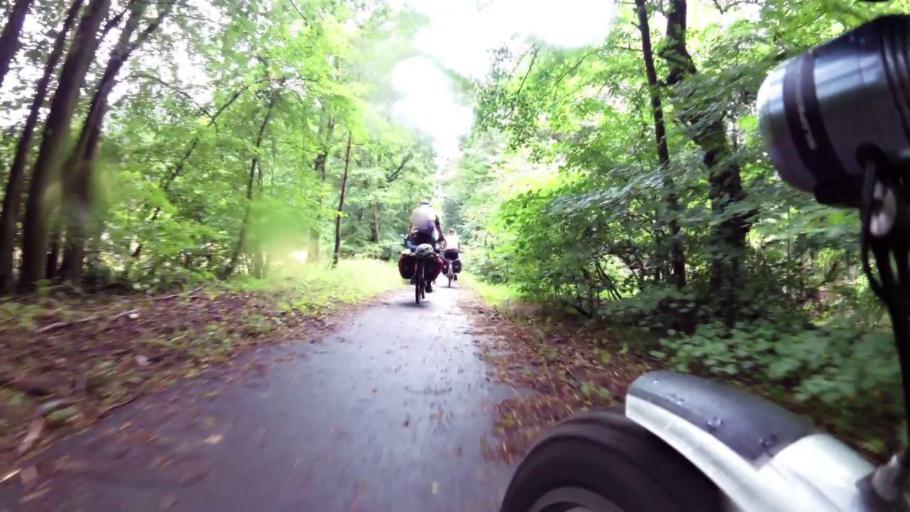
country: PL
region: West Pomeranian Voivodeship
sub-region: Powiat gryfinski
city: Banie
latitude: 53.0744
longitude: 14.6340
